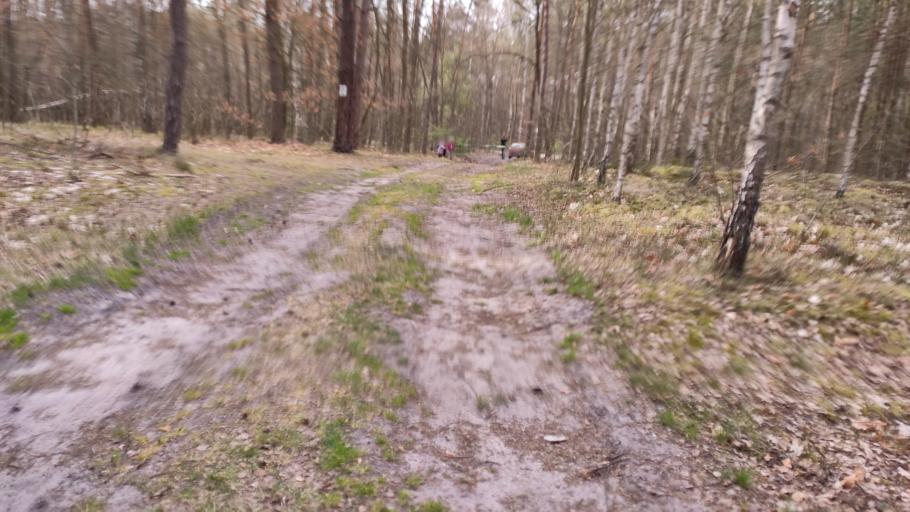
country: PL
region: Masovian Voivodeship
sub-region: Powiat grojecki
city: Warka
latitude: 51.7670
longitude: 21.1928
